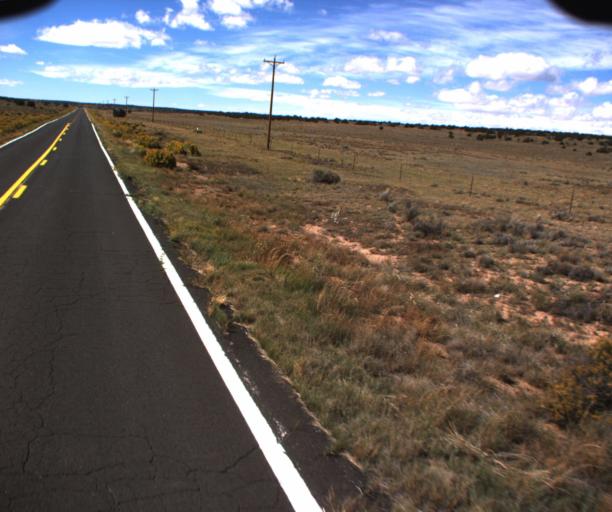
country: US
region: New Mexico
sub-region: McKinley County
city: Zuni Pueblo
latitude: 35.0143
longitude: -109.0598
